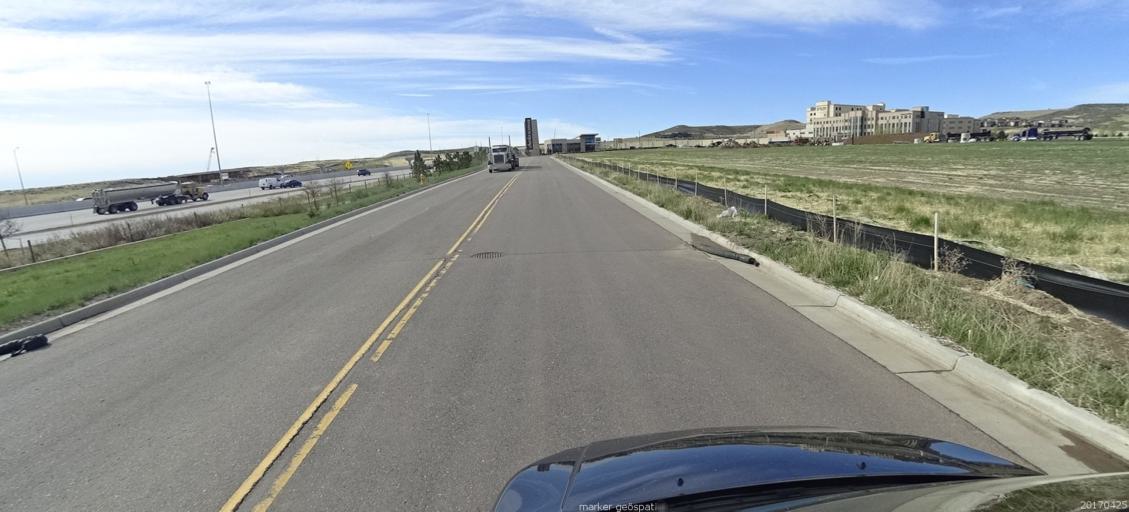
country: US
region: Colorado
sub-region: Douglas County
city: Meridian
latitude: 39.5341
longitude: -104.8692
